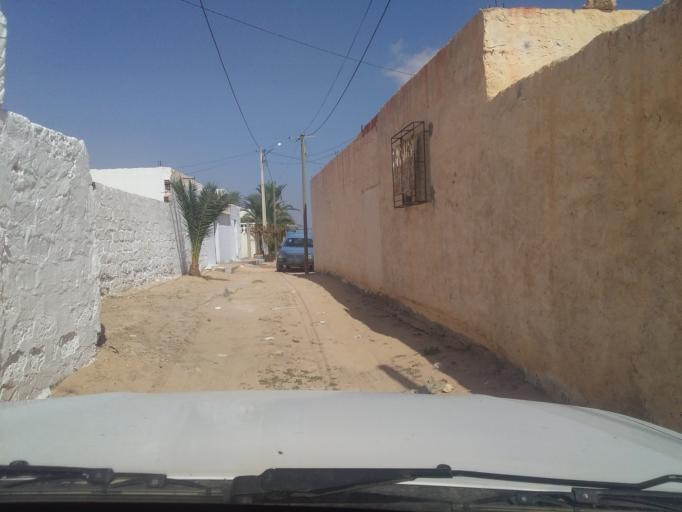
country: TN
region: Qabis
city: Gabes
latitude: 33.6250
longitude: 10.2796
